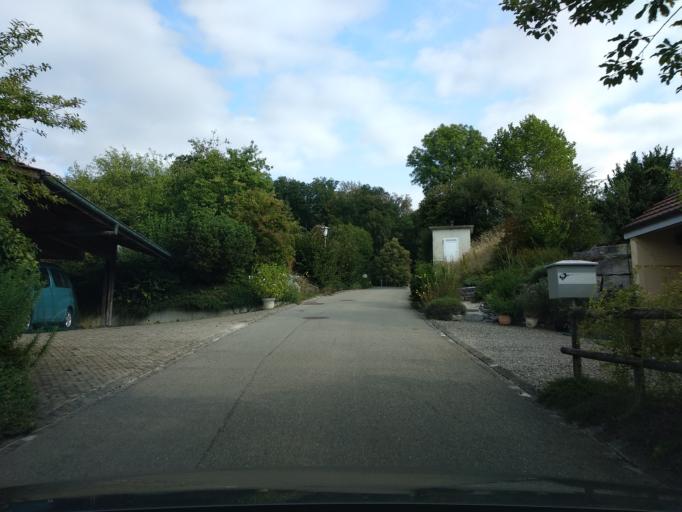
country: CH
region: Zurich
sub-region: Bezirk Andelfingen
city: Marthalen
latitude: 47.6532
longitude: 8.6767
